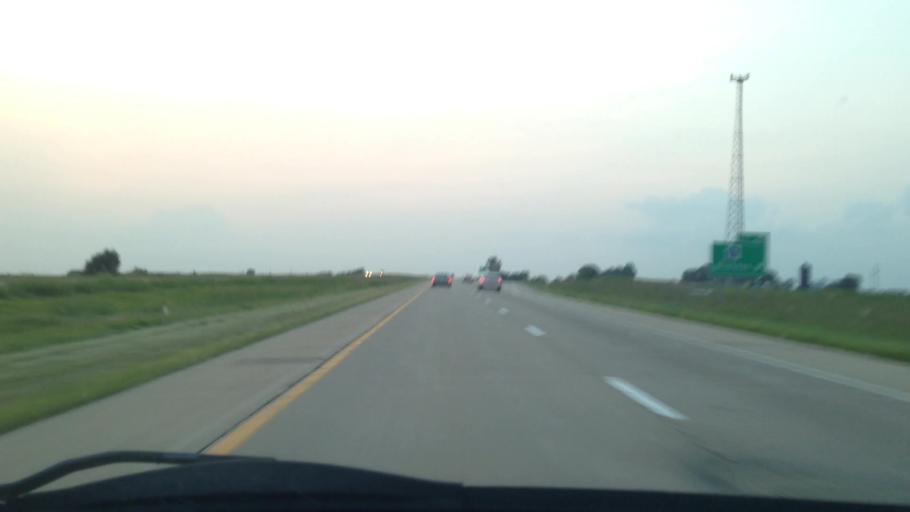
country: US
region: Iowa
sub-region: Benton County
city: Urbana
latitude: 42.3073
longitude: -91.9716
